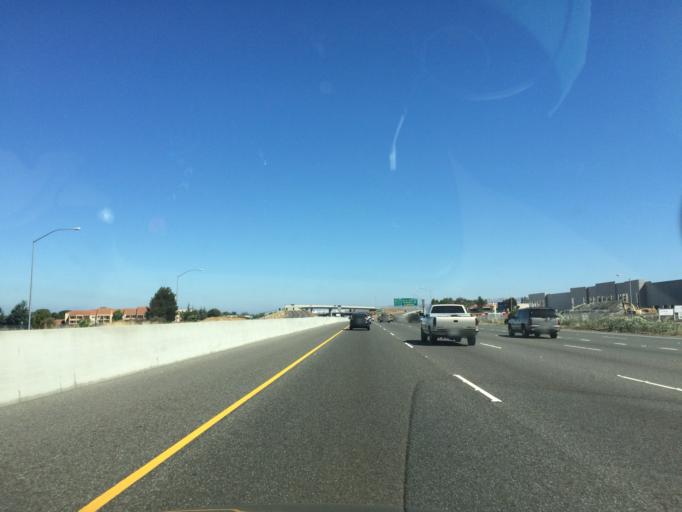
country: US
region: California
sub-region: Santa Clara County
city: Milpitas
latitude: 37.4759
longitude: -121.9323
